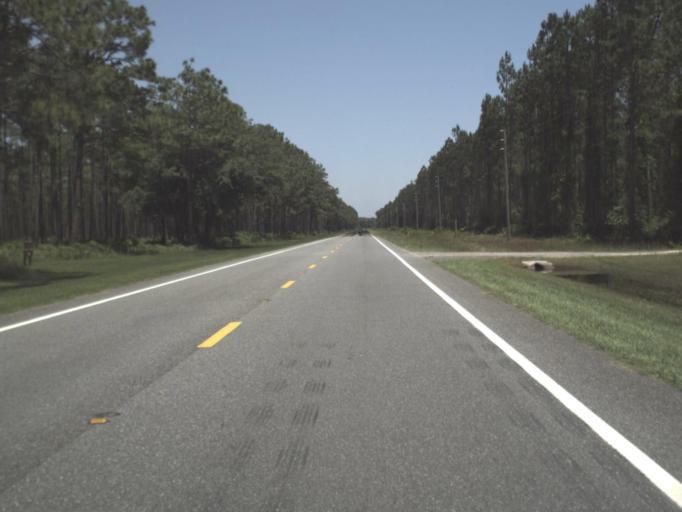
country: US
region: Florida
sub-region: Columbia County
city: Watertown
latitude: 30.1968
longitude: -82.4950
